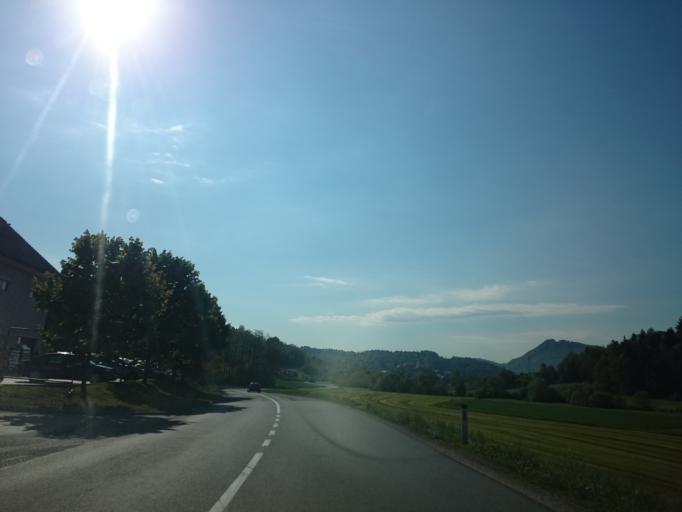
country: SI
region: Sentjur pri Celju
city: Sentjur
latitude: 46.2325
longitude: 15.3862
